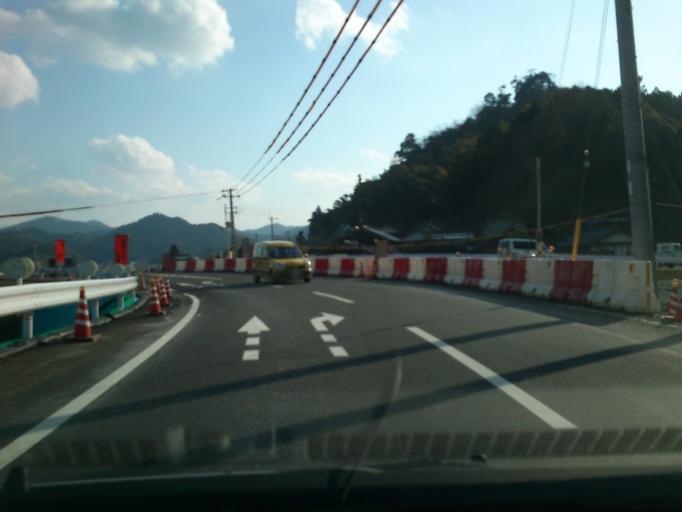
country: JP
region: Kyoto
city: Fukuchiyama
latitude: 35.4017
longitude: 135.1825
